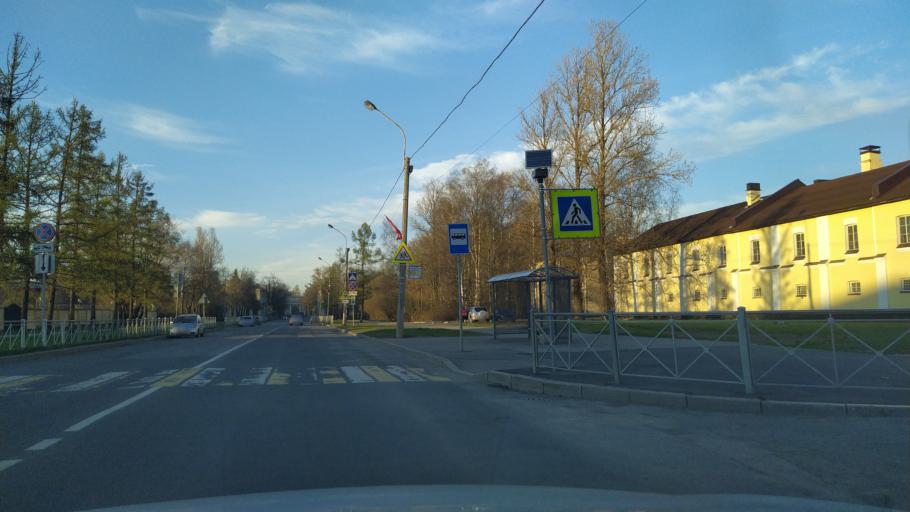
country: RU
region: St.-Petersburg
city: Pushkin
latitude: 59.7063
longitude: 30.3769
